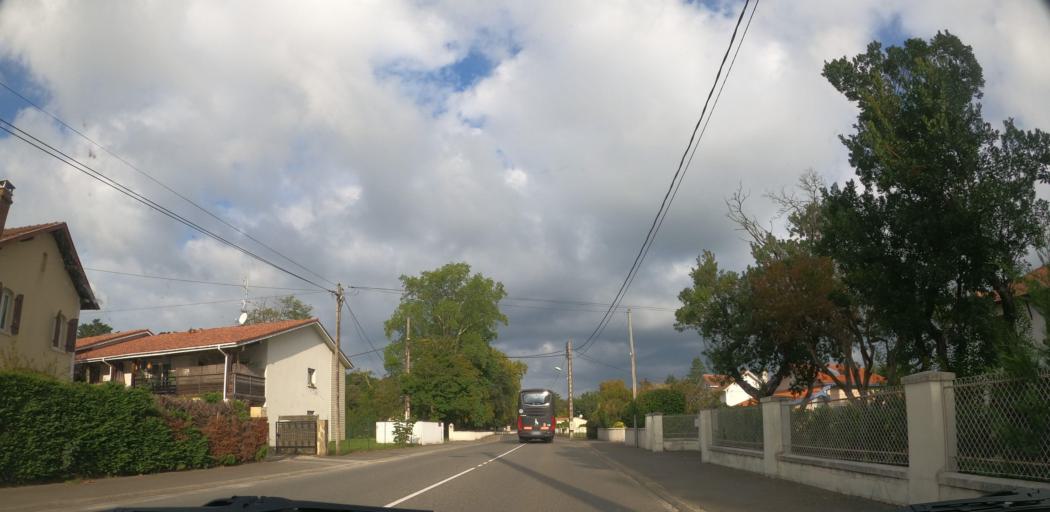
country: FR
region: Aquitaine
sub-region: Departement des Landes
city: Soustons
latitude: 43.7503
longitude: -1.3214
